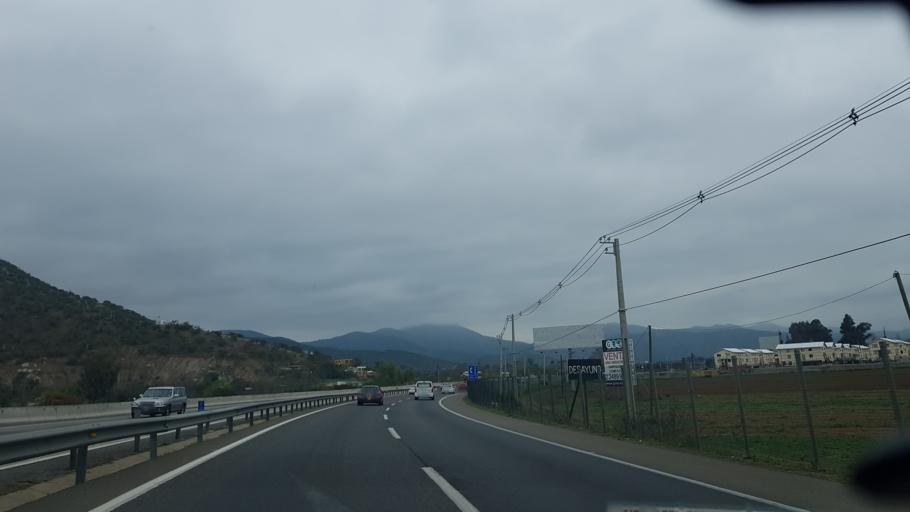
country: CL
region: Santiago Metropolitan
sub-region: Provincia de Chacabuco
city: Lampa
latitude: -33.4077
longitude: -71.1234
